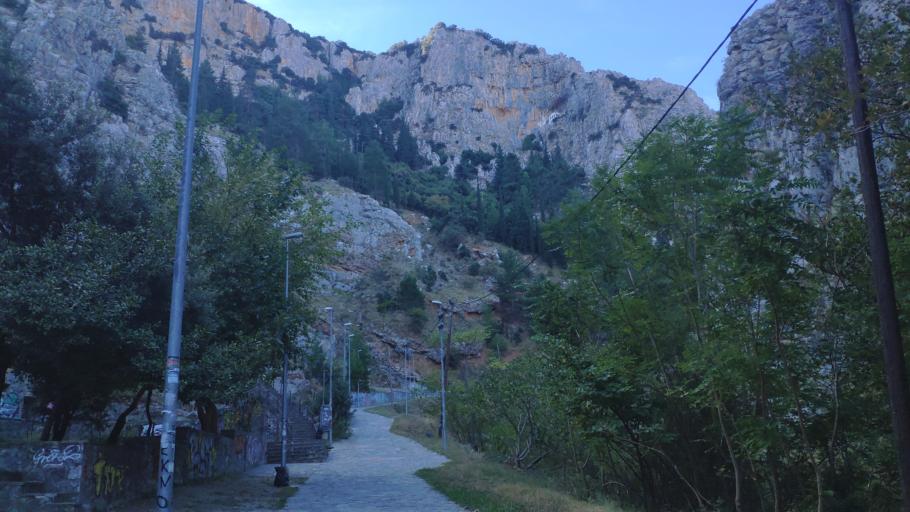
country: GR
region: Central Greece
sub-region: Nomos Voiotias
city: Livadeia
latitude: 38.4302
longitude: 22.8751
